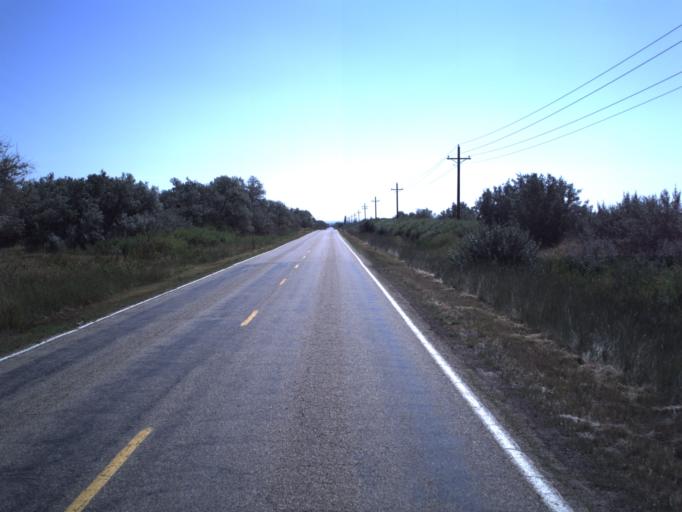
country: US
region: Utah
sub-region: Duchesne County
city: Roosevelt
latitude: 40.2580
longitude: -110.1913
